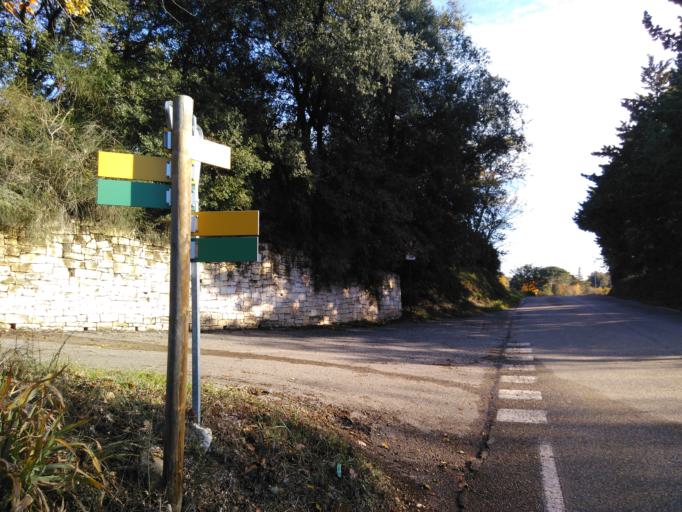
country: FR
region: Provence-Alpes-Cote d'Azur
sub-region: Departement du Vaucluse
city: Mondragon
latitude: 44.2346
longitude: 4.7233
